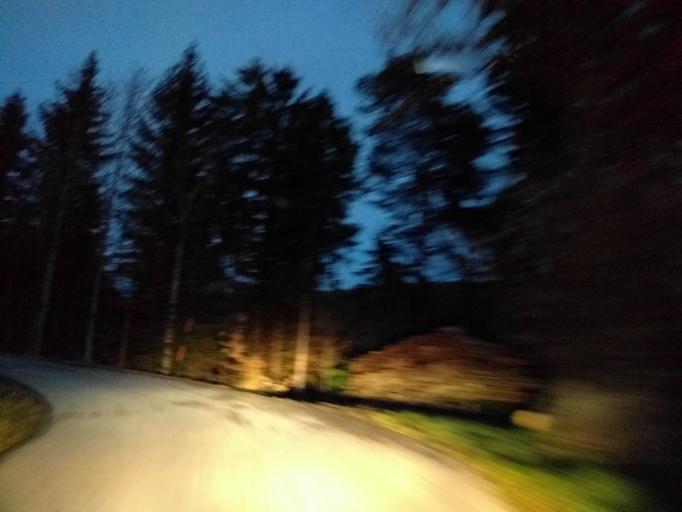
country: AT
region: Upper Austria
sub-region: Politischer Bezirk Urfahr-Umgebung
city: Kirchschlag bei Linz
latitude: 48.4053
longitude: 14.2939
